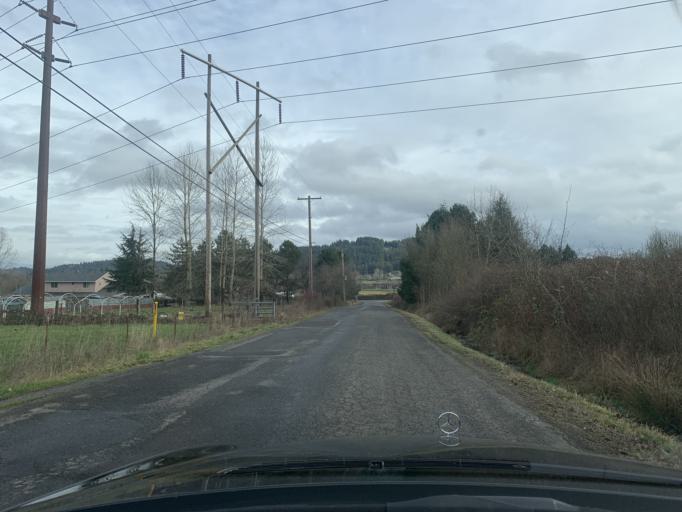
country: US
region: Oregon
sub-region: Clackamas County
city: Happy Valley
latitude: 45.4574
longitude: -122.4889
